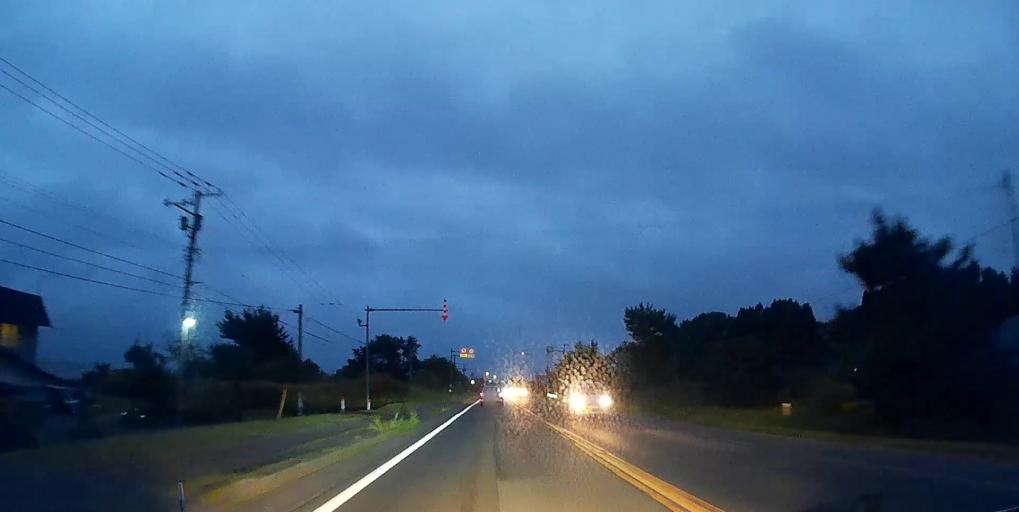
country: JP
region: Hokkaido
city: Nanae
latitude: 42.2226
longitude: 140.3666
